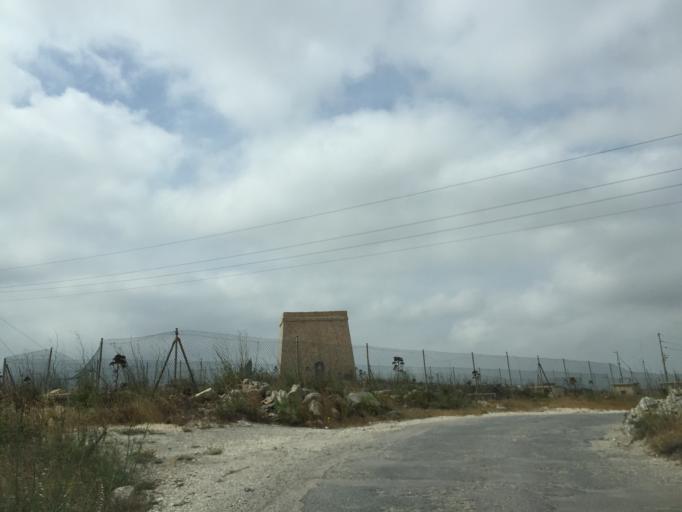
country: MT
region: L-Imgarr
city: Imgarr
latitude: 35.9001
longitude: 14.3713
